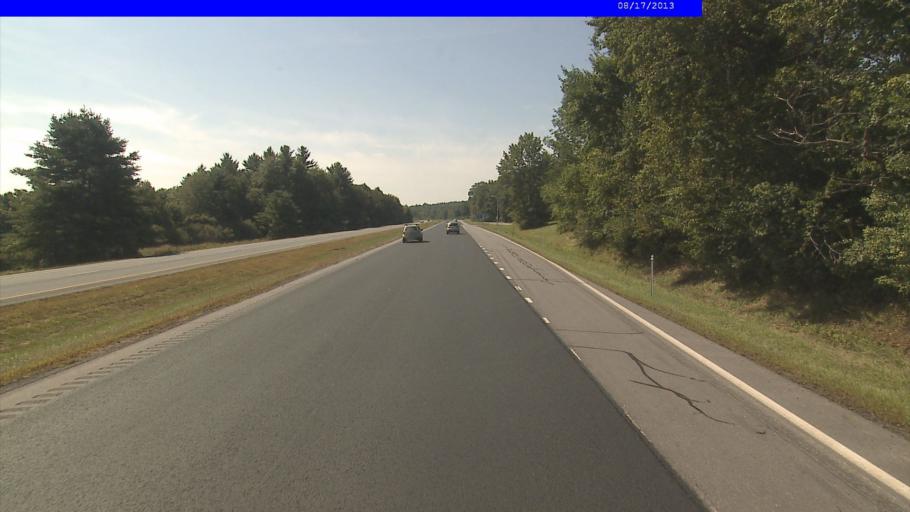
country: US
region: New Hampshire
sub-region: Cheshire County
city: Westmoreland
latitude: 43.0262
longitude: -72.4716
